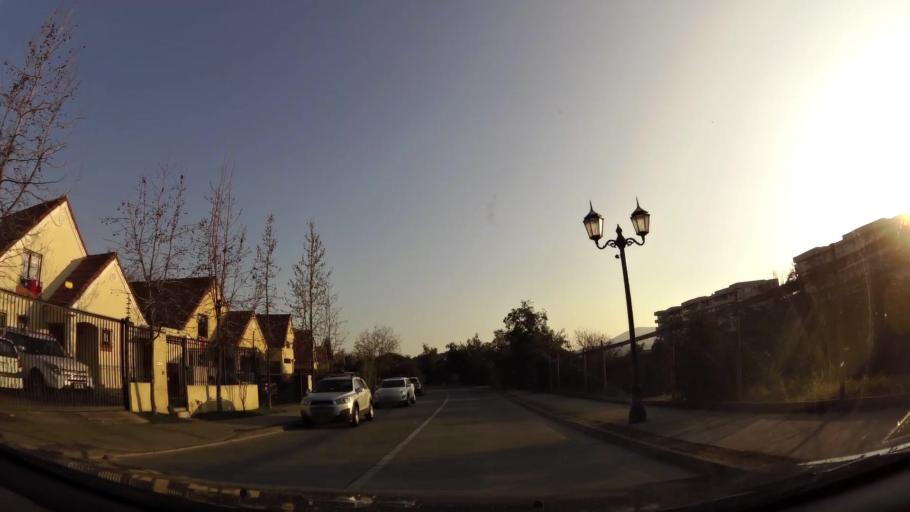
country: CL
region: Santiago Metropolitan
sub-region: Provincia de Santiago
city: Villa Presidente Frei, Nunoa, Santiago, Chile
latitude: -33.3311
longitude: -70.5085
